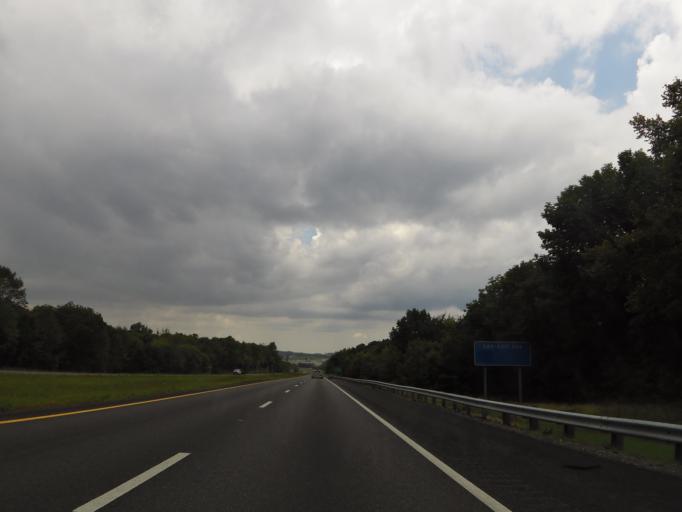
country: US
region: Tennessee
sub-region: Wilson County
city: Watertown
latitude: 36.1836
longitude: -86.1557
